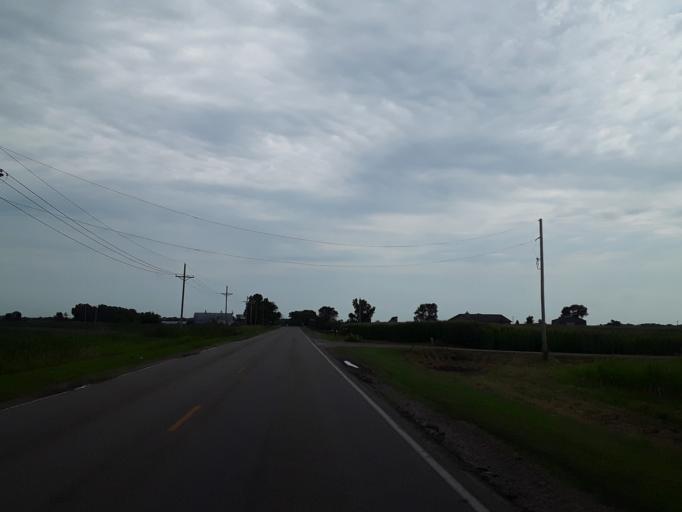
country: US
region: Nebraska
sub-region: Saunders County
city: Yutan
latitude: 41.2230
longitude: -96.3303
